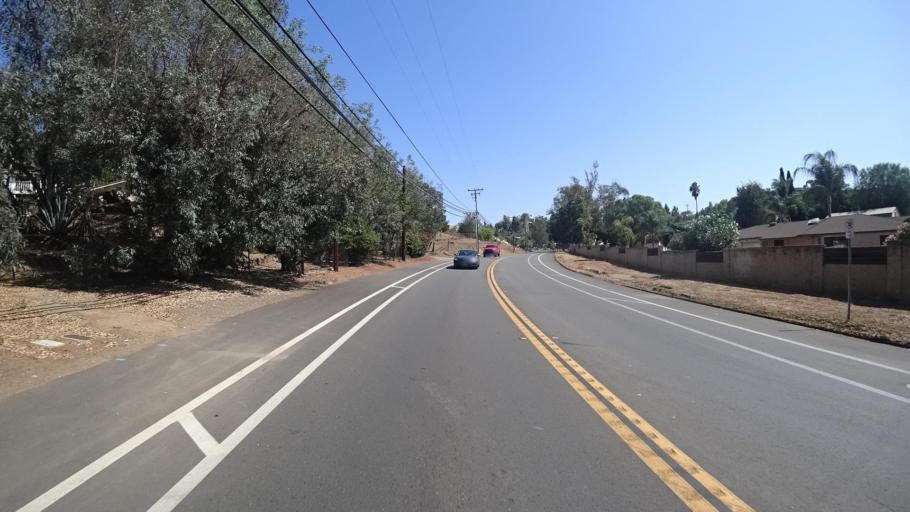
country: US
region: California
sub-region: San Diego County
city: Granite Hills
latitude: 32.7872
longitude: -116.9153
